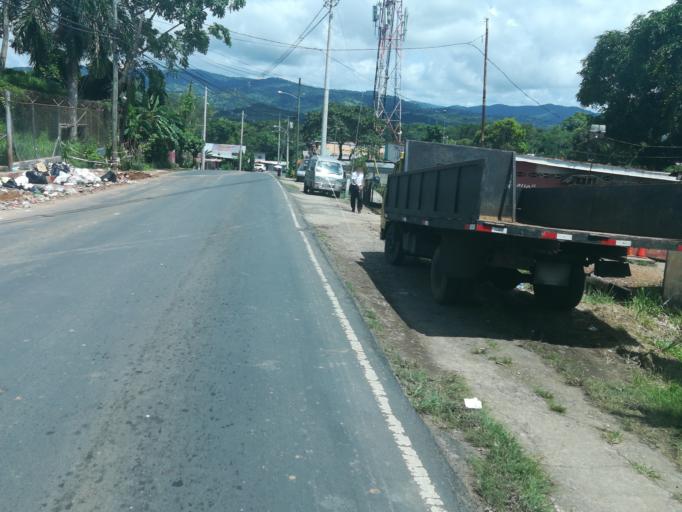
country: PA
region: Panama
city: Tocumen
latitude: 9.0918
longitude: -79.4074
